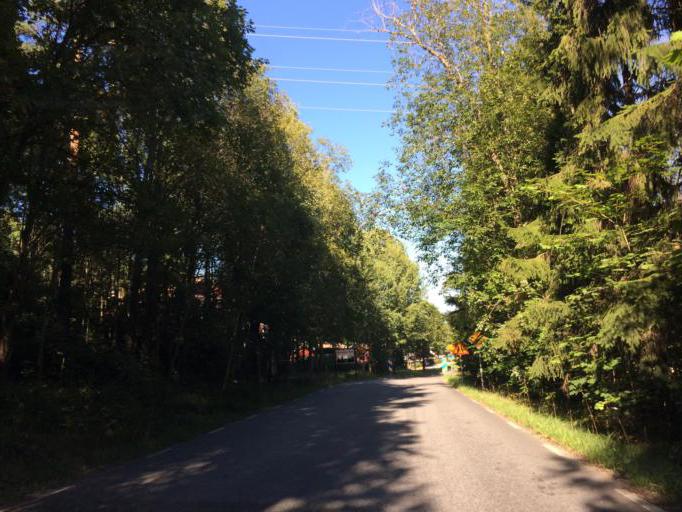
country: SE
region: Stockholm
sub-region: Upplands Vasby Kommun
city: Upplands Vaesby
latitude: 59.4881
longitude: 17.9422
